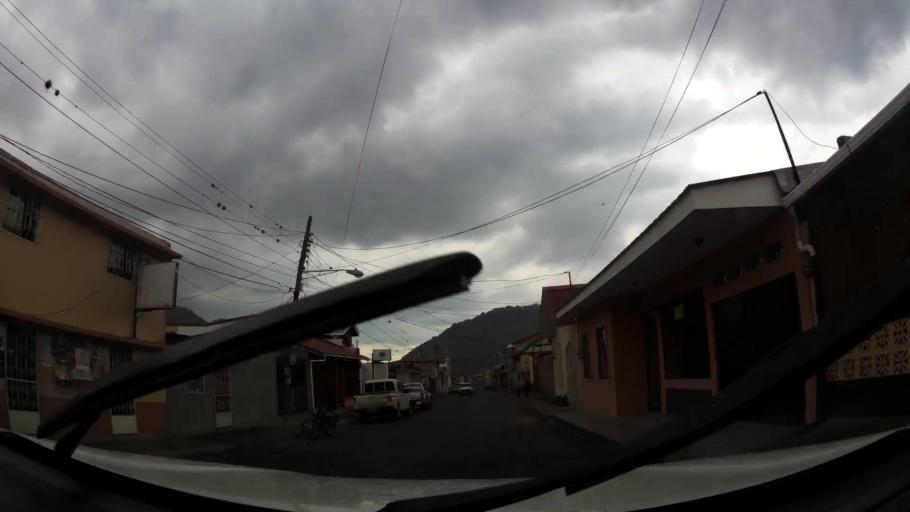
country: NI
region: Jinotega
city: Jinotega
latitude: 13.0901
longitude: -86.0001
